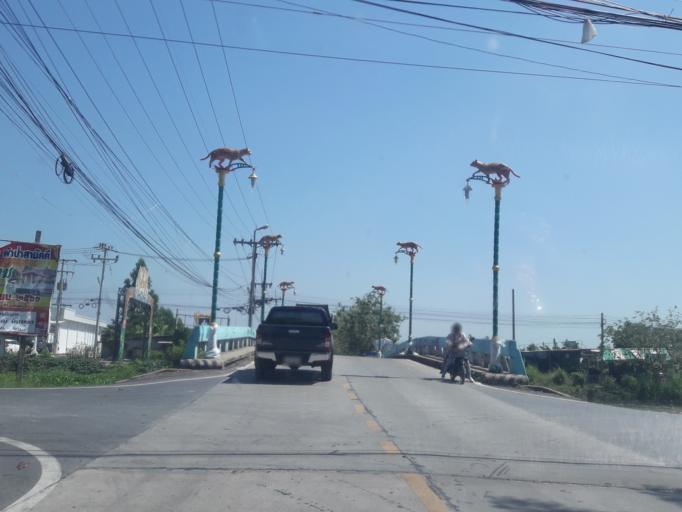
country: TH
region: Pathum Thani
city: Nong Suea
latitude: 14.1360
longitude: 100.8684
